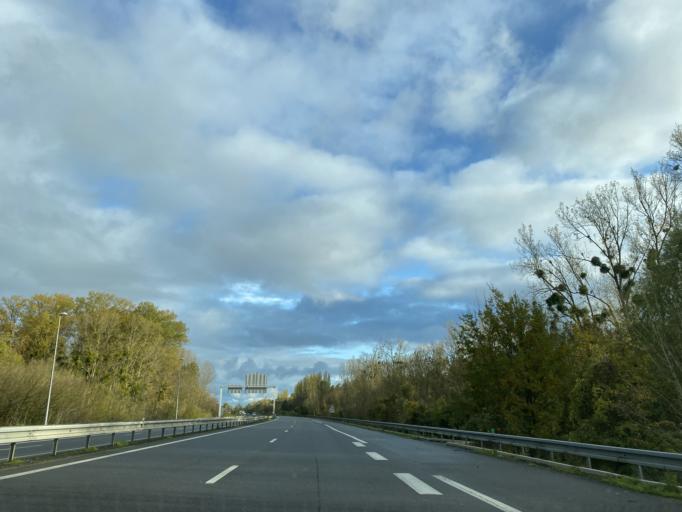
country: FR
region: Centre
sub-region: Departement du Cher
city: Vierzon
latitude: 47.2060
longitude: 2.1226
